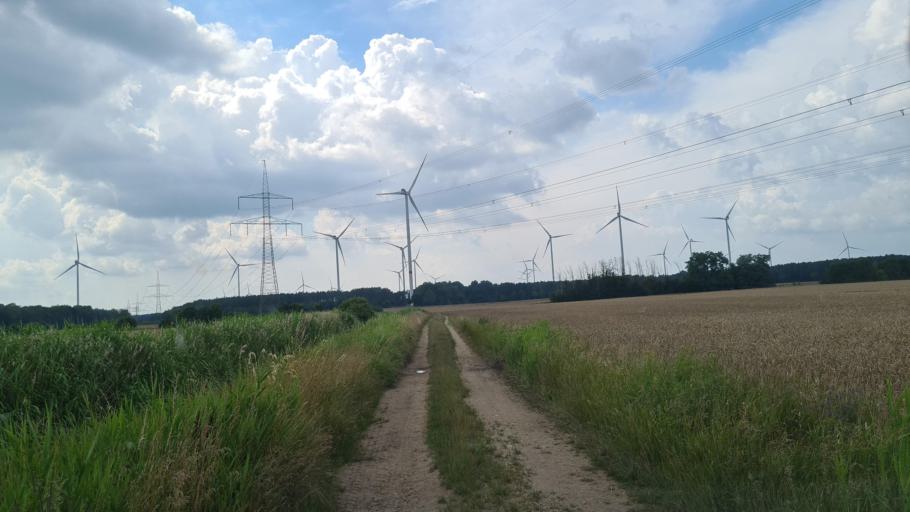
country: DE
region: Brandenburg
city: Sallgast
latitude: 51.6273
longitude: 13.8505
